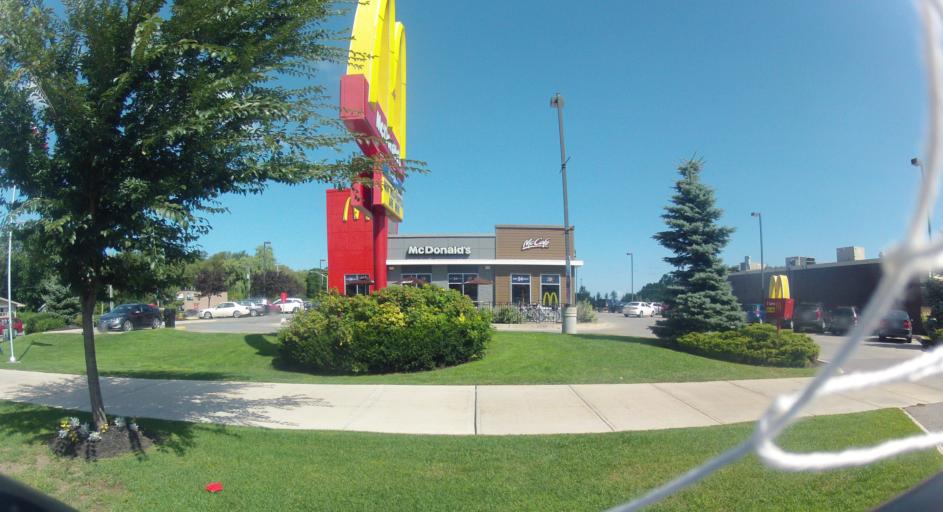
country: CA
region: Ontario
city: Collingwood
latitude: 44.5020
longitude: -80.2262
